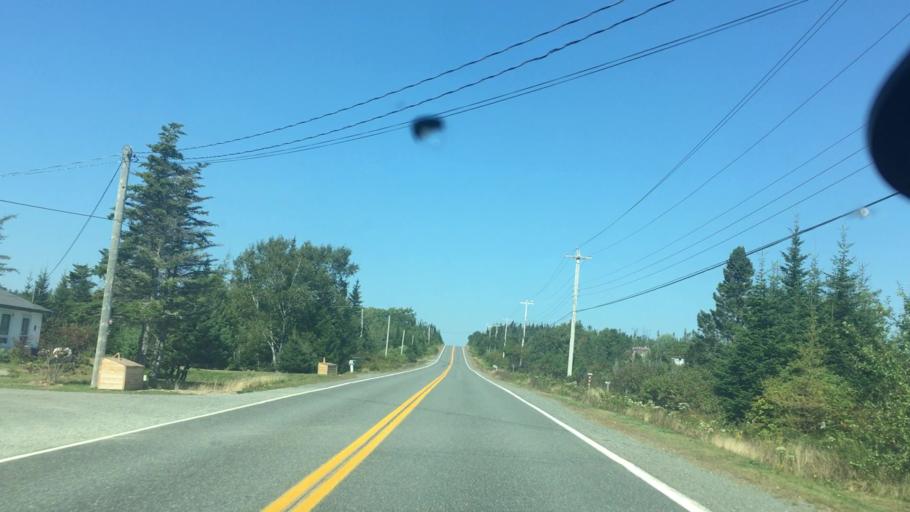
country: CA
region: Nova Scotia
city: Antigonish
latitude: 45.0010
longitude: -62.1000
